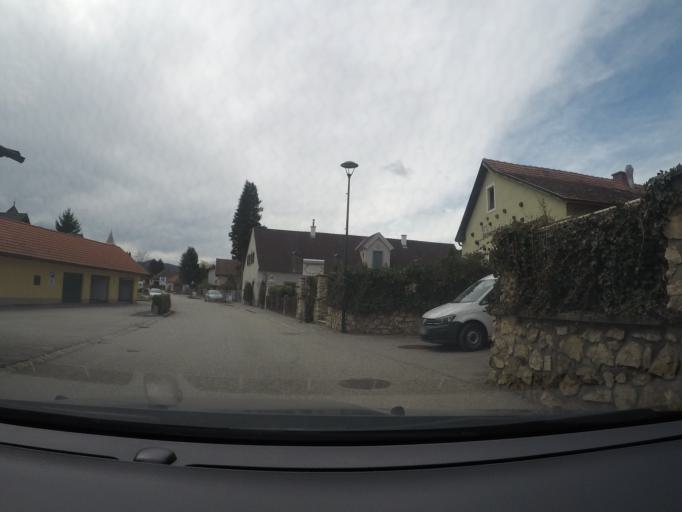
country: AT
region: Lower Austria
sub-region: Politischer Bezirk Neunkirchen
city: Pitten
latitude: 47.7251
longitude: 16.1889
